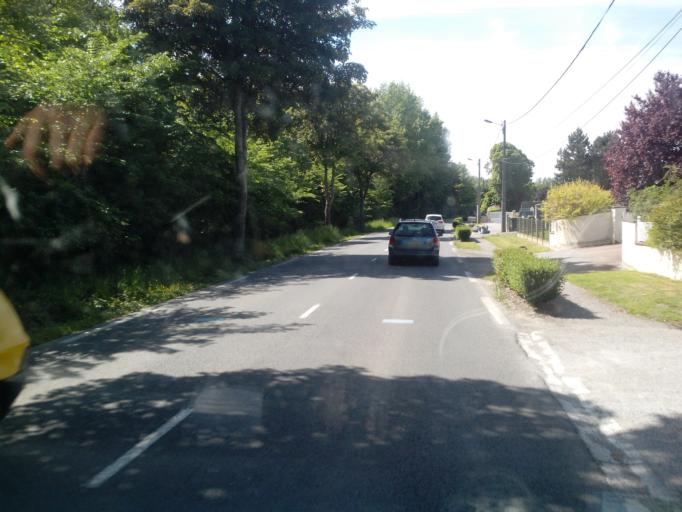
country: FR
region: Nord-Pas-de-Calais
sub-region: Departement du Pas-de-Calais
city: Saint-Josse
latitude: 50.4988
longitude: 1.6962
